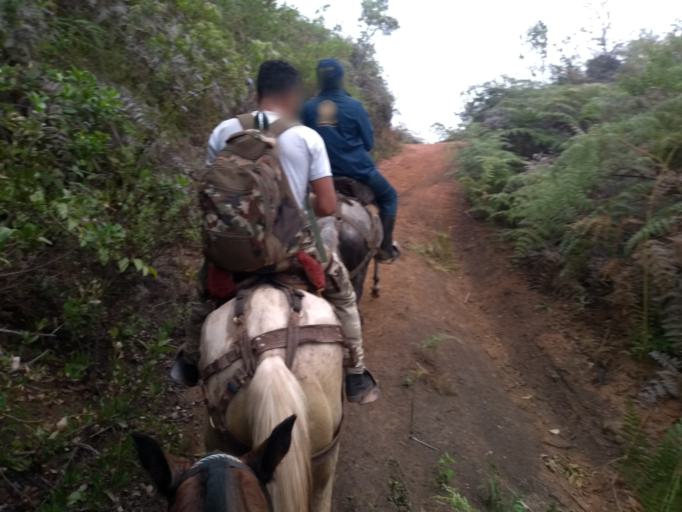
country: CO
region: Cesar
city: San Diego
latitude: 10.1793
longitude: -73.0426
